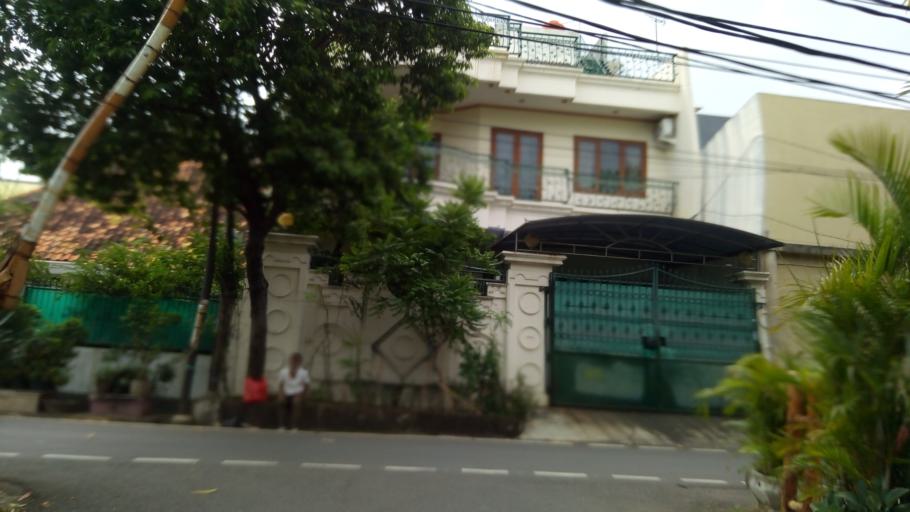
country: ID
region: Jakarta Raya
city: Jakarta
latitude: -6.1546
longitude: 106.8347
